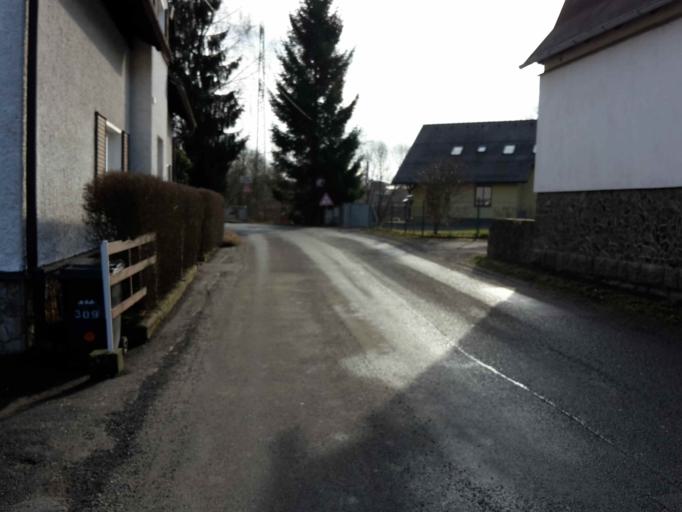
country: CZ
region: Liberecky
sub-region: Okres Liberec
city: Liberec
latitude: 50.7463
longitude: 15.0731
